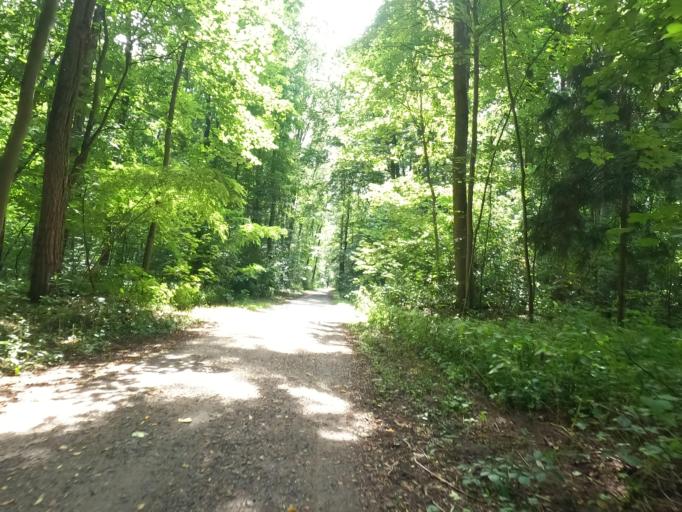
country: DE
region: Hesse
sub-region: Regierungsbezirk Darmstadt
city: Offenbach
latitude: 50.0871
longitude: 8.7278
